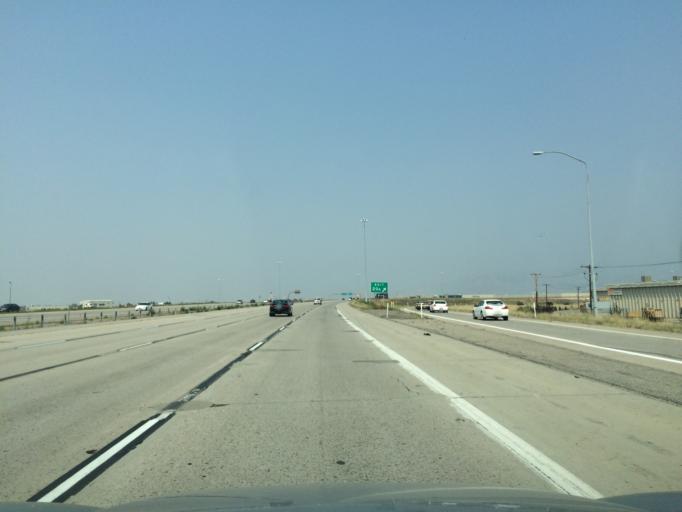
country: US
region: Utah
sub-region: Salt Lake County
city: Taylorsville
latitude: 40.7202
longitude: -111.9527
